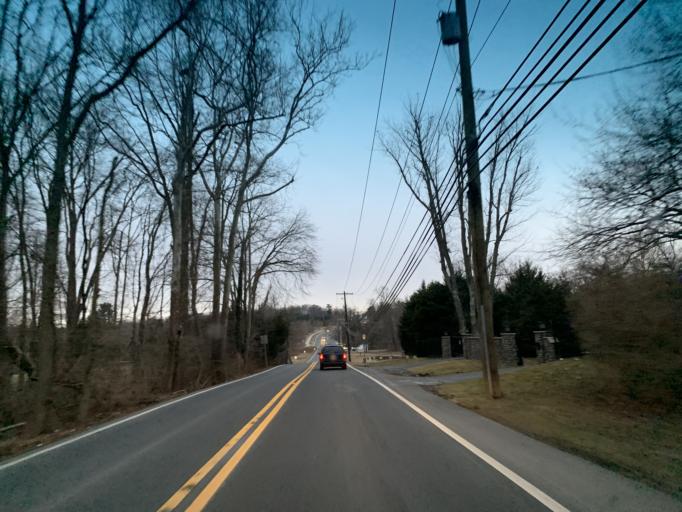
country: US
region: Maryland
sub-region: Montgomery County
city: Layhill
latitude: 39.1043
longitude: -77.0392
